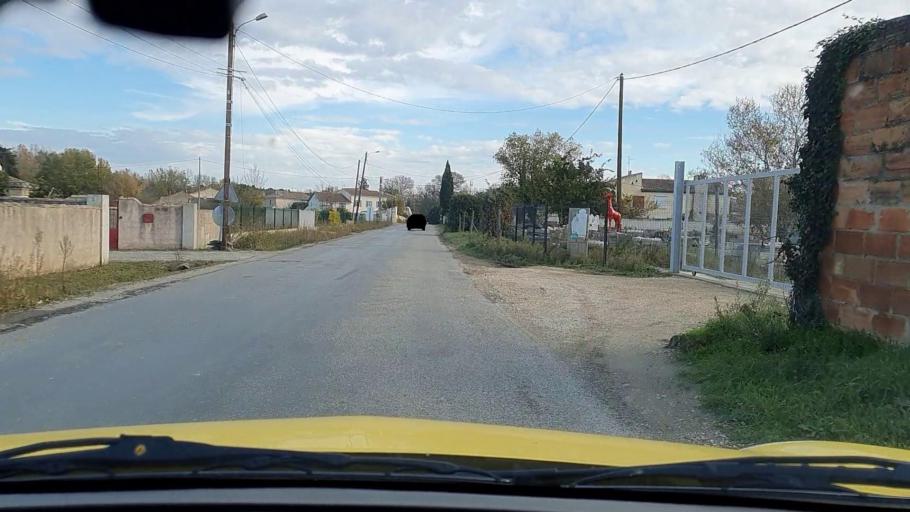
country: FR
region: Languedoc-Roussillon
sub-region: Departement du Gard
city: Montfrin
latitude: 43.8706
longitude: 4.5850
